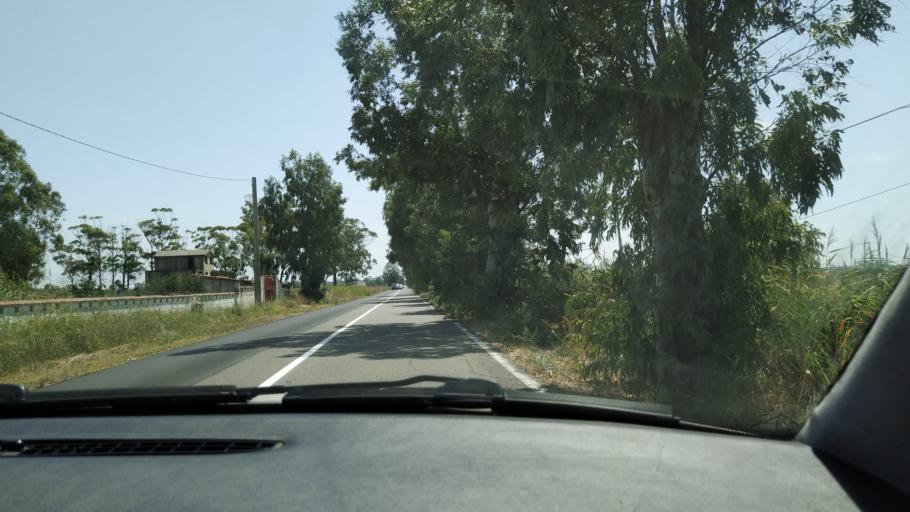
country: IT
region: Basilicate
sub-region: Provincia di Matera
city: Marconia
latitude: 40.3330
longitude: 16.7781
